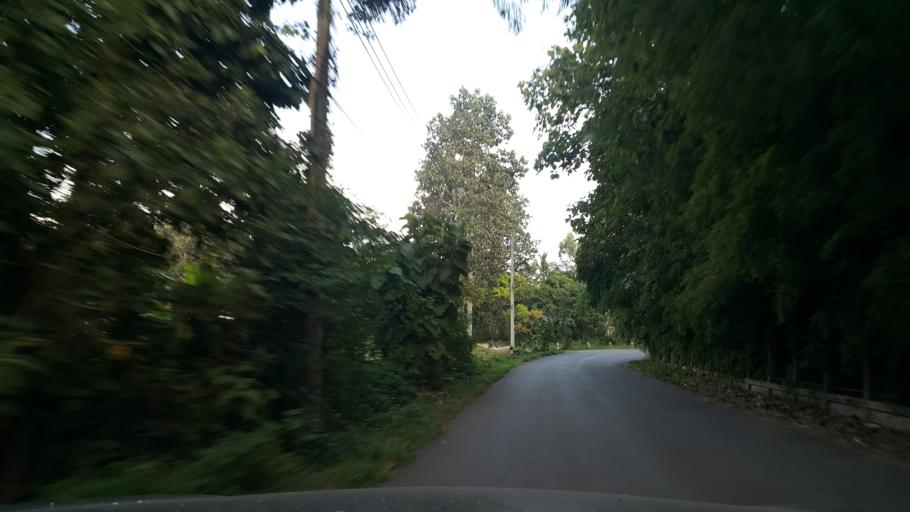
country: TH
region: Chiang Mai
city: San Sai
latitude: 18.9079
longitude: 99.0399
